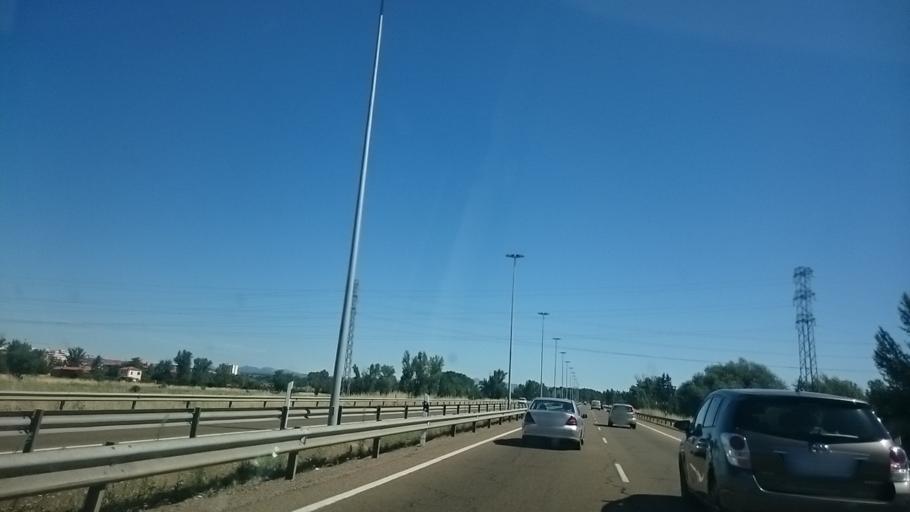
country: ES
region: Castille and Leon
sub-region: Provincia de Leon
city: Leon
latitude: 42.5904
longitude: -5.5539
